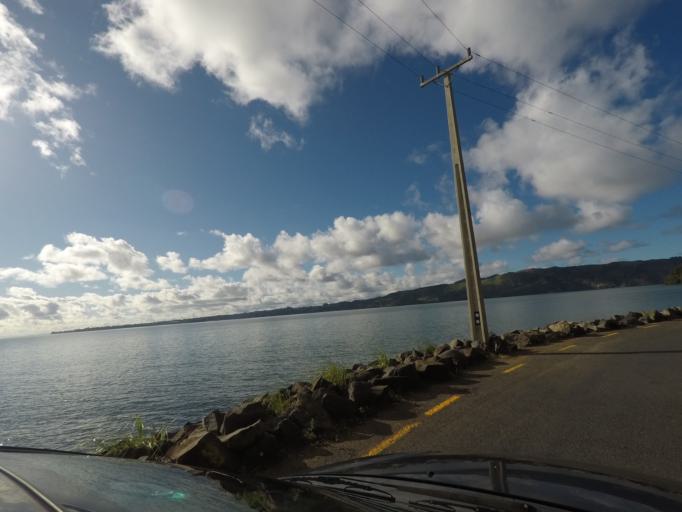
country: NZ
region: Auckland
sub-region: Auckland
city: Titirangi
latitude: -37.0116
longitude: 174.5618
